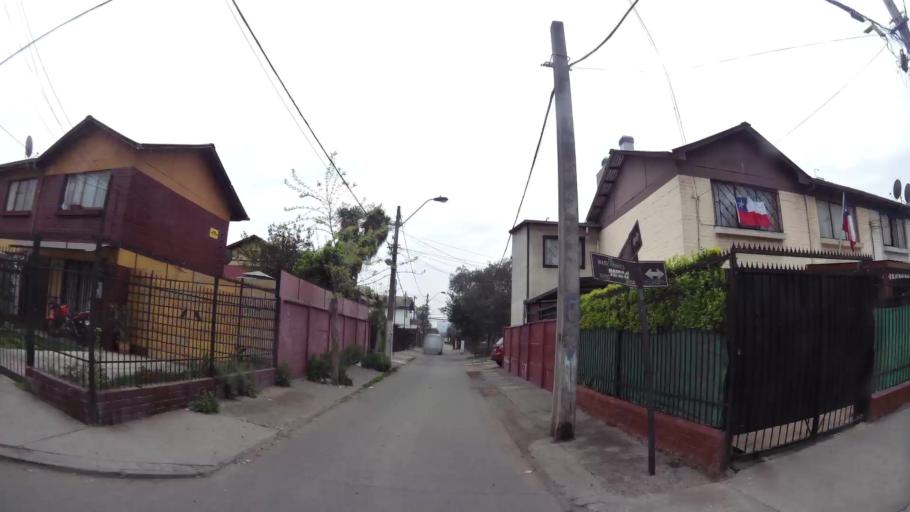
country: CL
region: Santiago Metropolitan
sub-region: Provincia de Santiago
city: Villa Presidente Frei, Nunoa, Santiago, Chile
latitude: -33.5030
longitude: -70.6022
